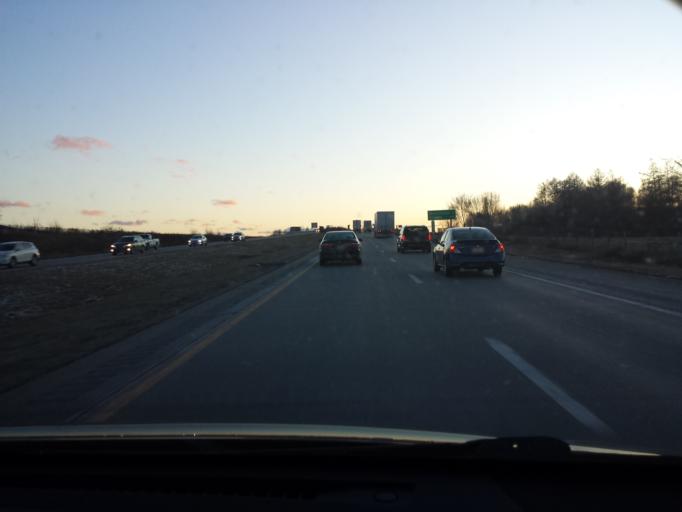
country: US
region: Pennsylvania
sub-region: Centre County
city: Pleasant Gap
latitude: 40.8610
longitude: -77.7904
